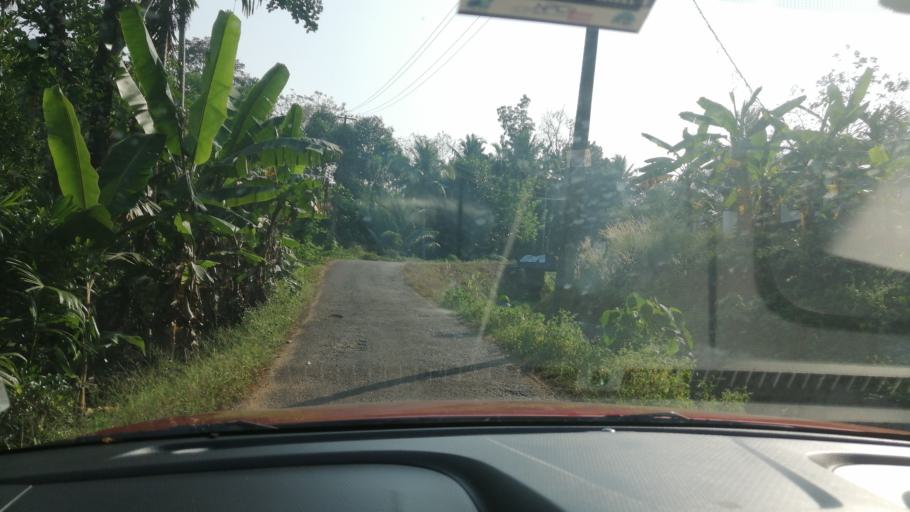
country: IN
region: Kerala
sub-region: Ernakulam
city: Piravam
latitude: 9.8929
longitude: 76.4436
